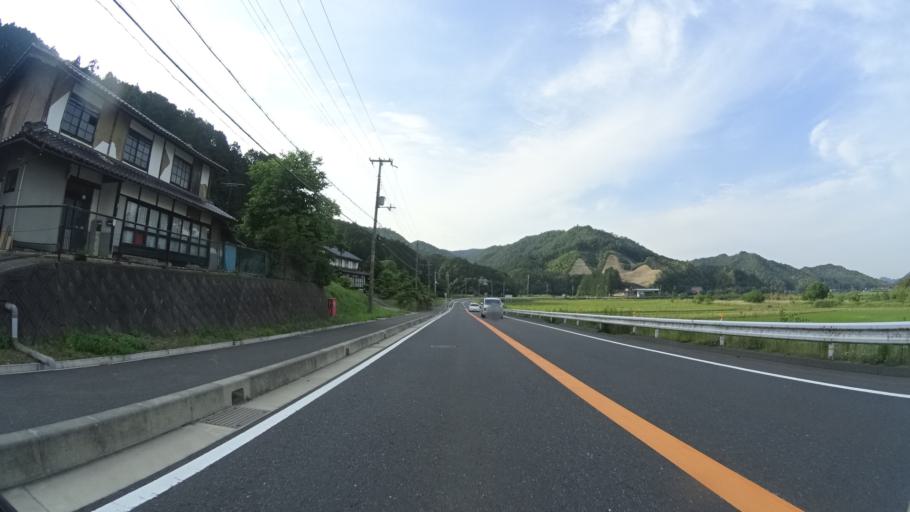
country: JP
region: Kyoto
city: Fukuchiyama
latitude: 35.4023
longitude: 135.1825
